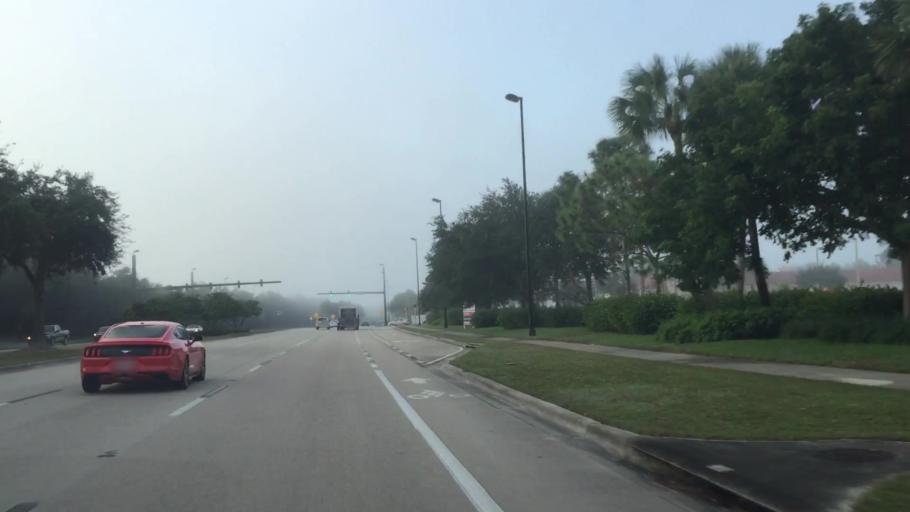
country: US
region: Florida
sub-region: Lee County
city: Three Oaks
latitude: 26.4835
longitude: -81.7849
